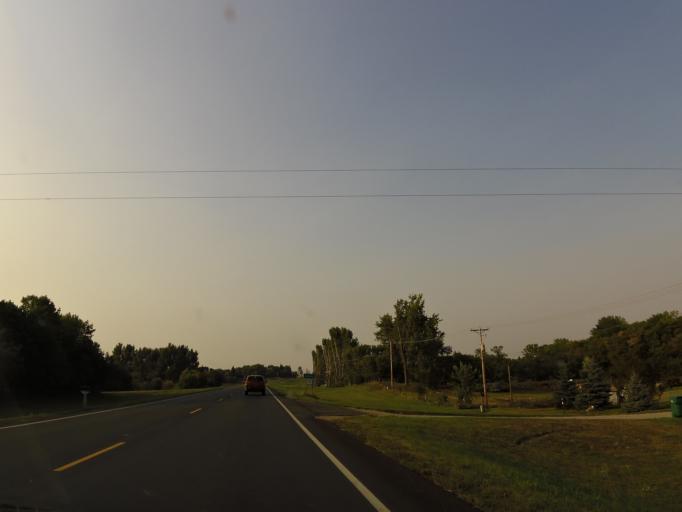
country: US
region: North Dakota
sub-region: Traill County
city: Mayville
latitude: 47.4906
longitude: -97.3233
